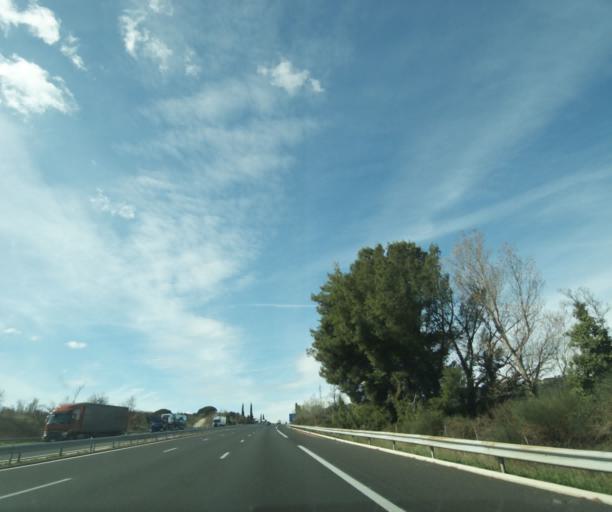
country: FR
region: Languedoc-Roussillon
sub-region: Departement du Gard
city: Sernhac
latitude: 43.9047
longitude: 4.5520
